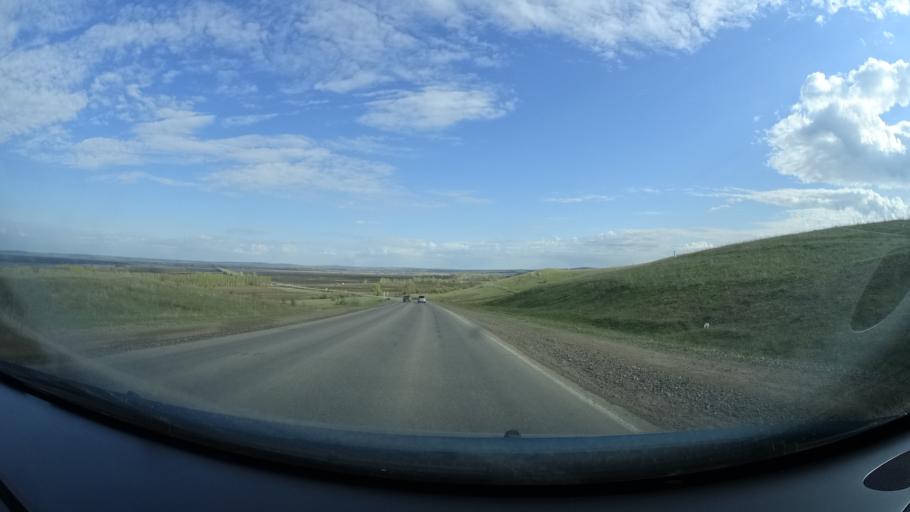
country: RU
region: Bashkortostan
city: Blagoveshchensk
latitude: 55.1785
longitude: 55.8537
